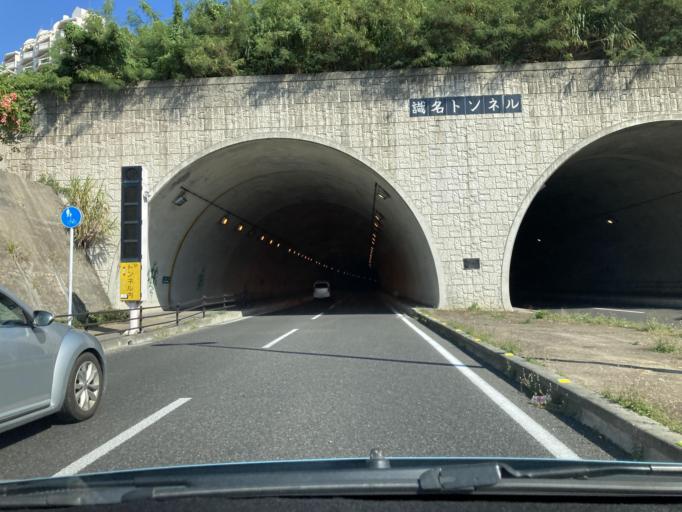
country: JP
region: Okinawa
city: Naha-shi
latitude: 26.2032
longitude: 127.7076
